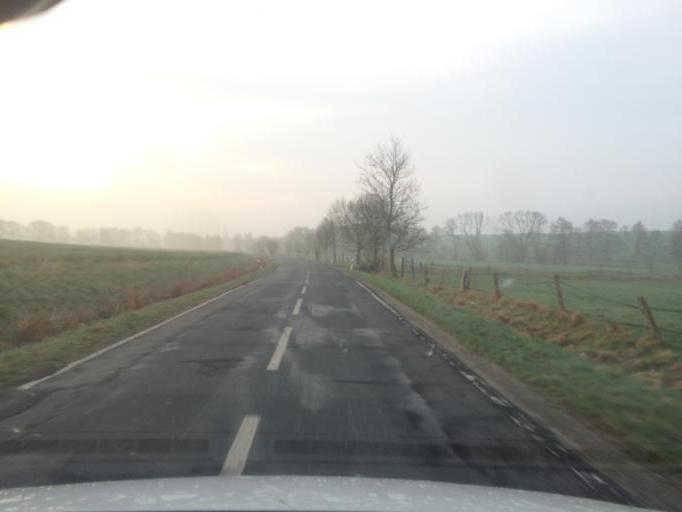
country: DE
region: Thuringia
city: Bischofferode
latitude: 51.5308
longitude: 10.4860
